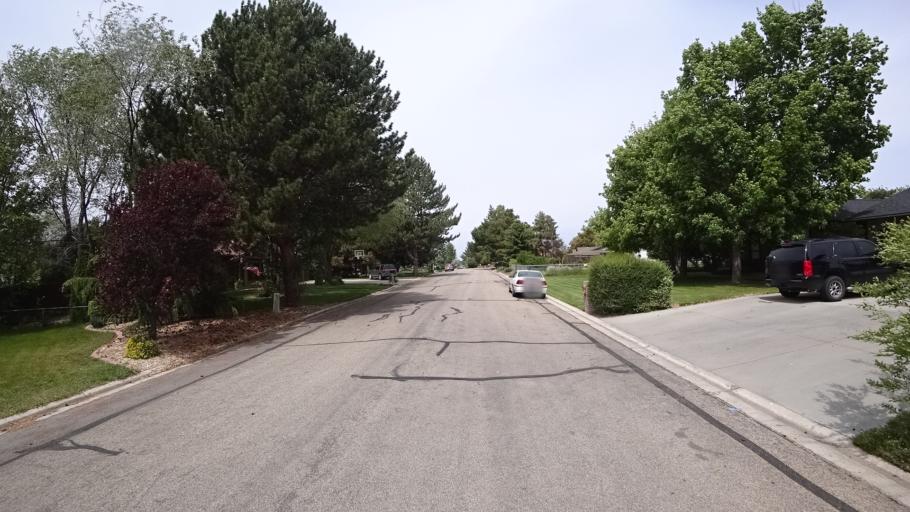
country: US
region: Idaho
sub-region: Ada County
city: Meridian
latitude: 43.5556
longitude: -116.3251
